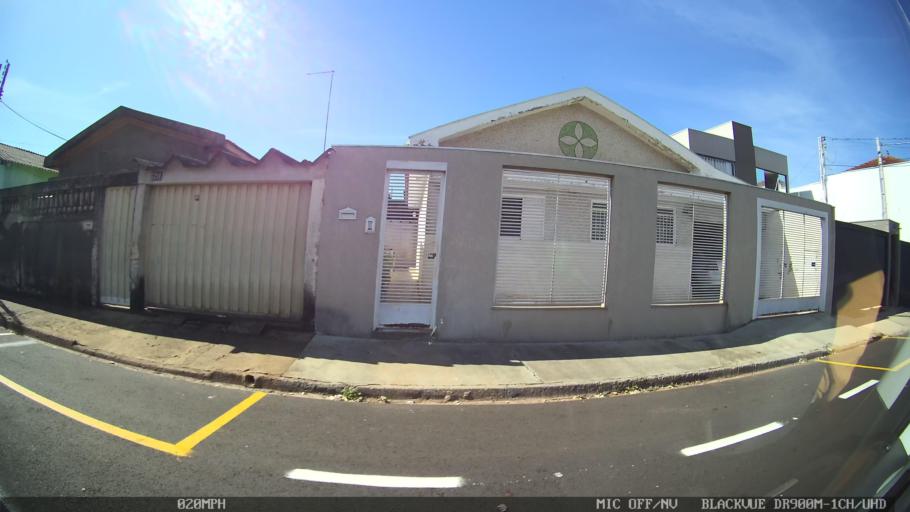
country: BR
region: Sao Paulo
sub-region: Franca
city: Franca
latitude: -20.5469
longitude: -47.3889
